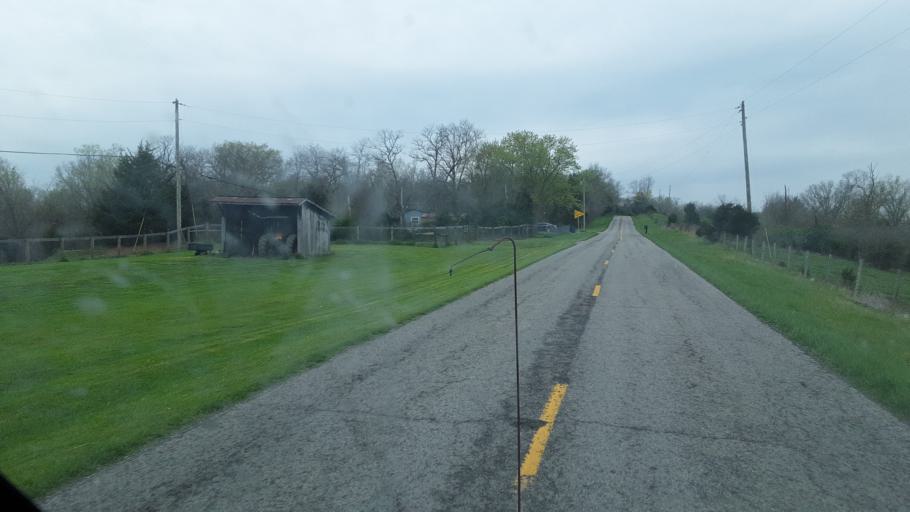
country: US
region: Kentucky
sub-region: Grant County
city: Dry Ridge
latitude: 38.6462
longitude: -84.7321
